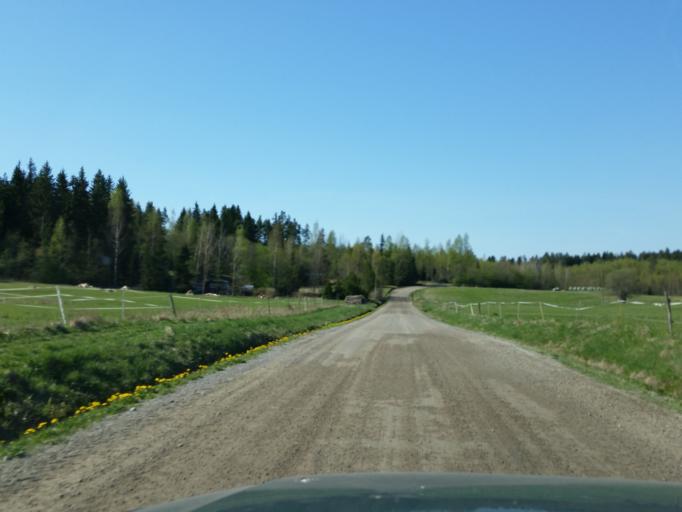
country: FI
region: Uusimaa
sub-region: Helsinki
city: Karjalohja
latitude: 60.1431
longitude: 23.7674
